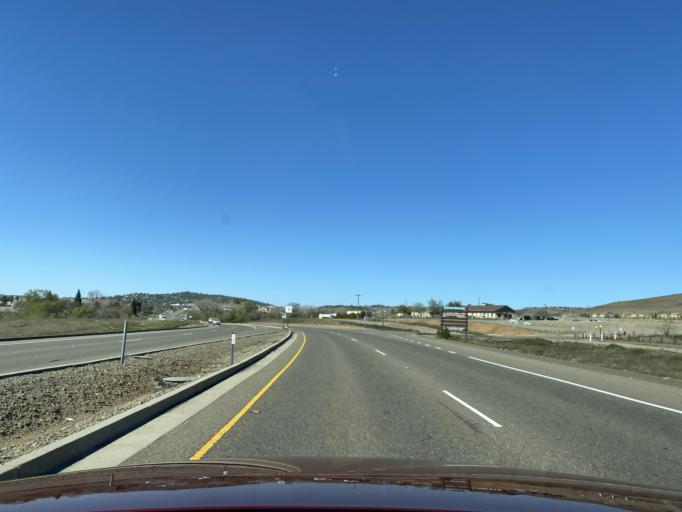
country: US
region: California
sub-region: El Dorado County
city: El Dorado Hills
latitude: 38.6330
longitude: -121.0589
